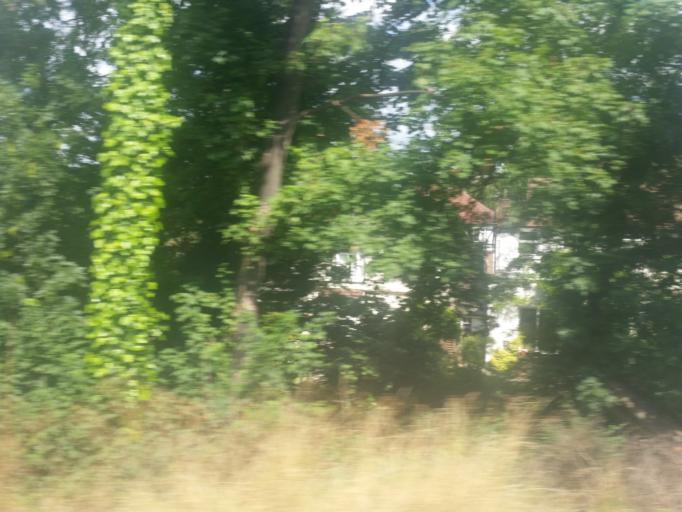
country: GB
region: England
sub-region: Greater London
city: Thornton Heath
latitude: 51.4262
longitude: -0.0886
